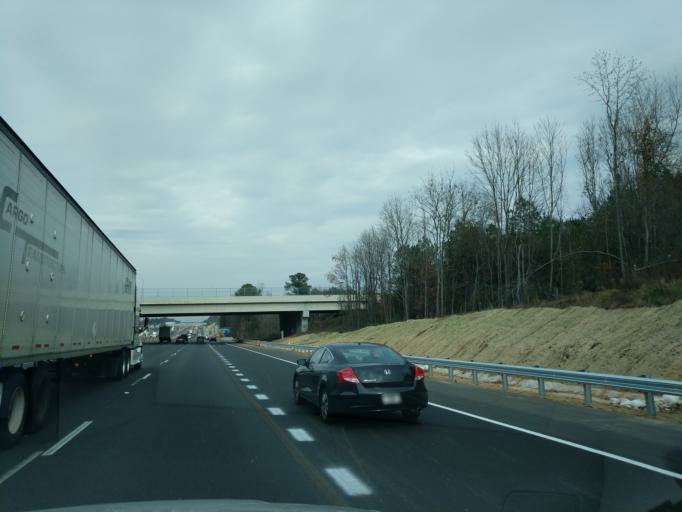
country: US
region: Georgia
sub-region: Gwinnett County
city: Suwanee
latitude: 34.0217
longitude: -84.0586
